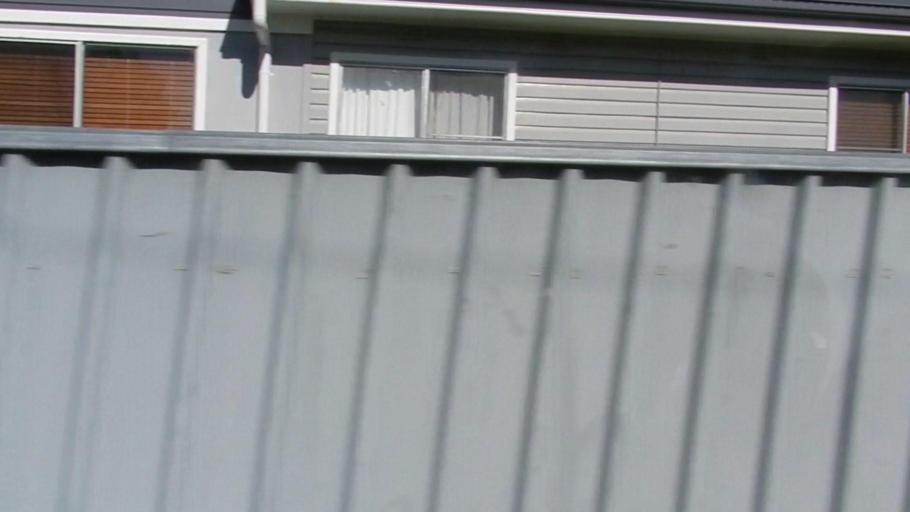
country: AU
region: New South Wales
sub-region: Tamworth Municipality
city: Manilla
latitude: -30.3784
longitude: 150.6093
